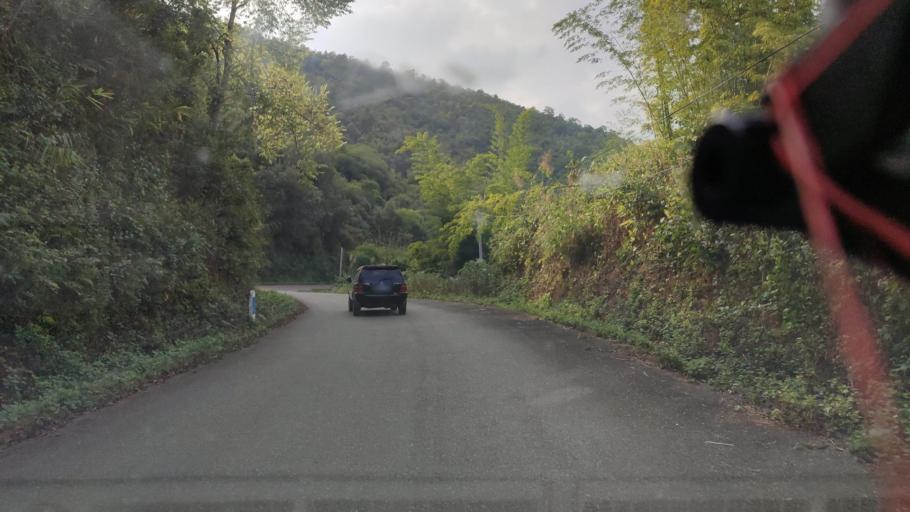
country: CN
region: Yunnan
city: Menghai
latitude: 21.4855
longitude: 99.7393
